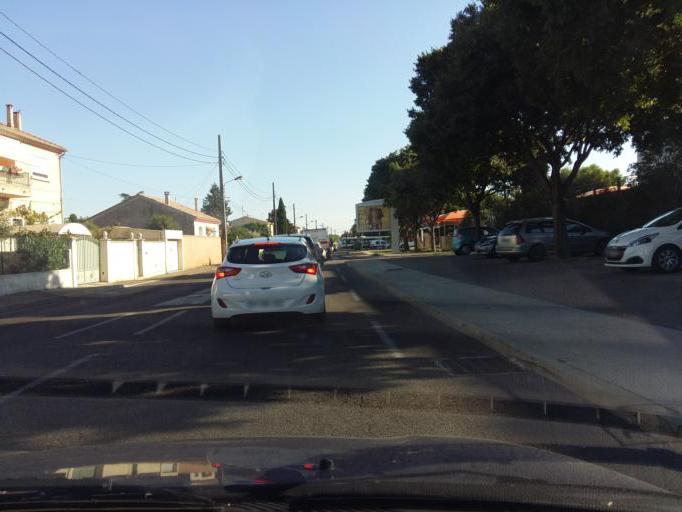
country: FR
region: Languedoc-Roussillon
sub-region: Departement du Gard
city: Nimes
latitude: 43.8181
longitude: 4.3527
